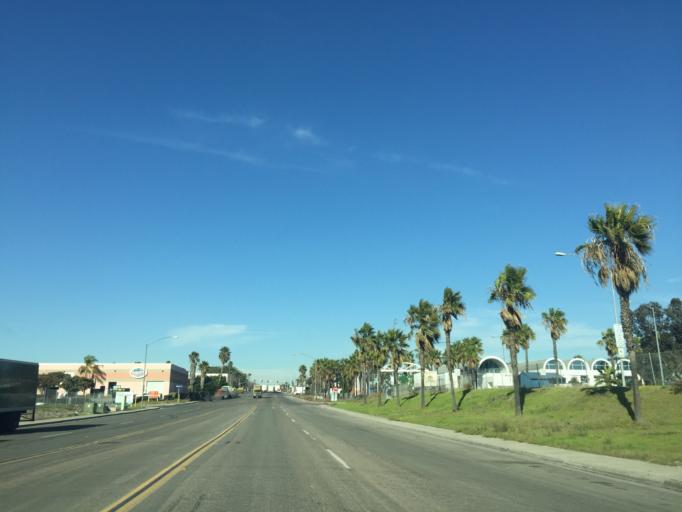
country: MX
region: Baja California
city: Tijuana
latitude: 32.5533
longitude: -116.9278
